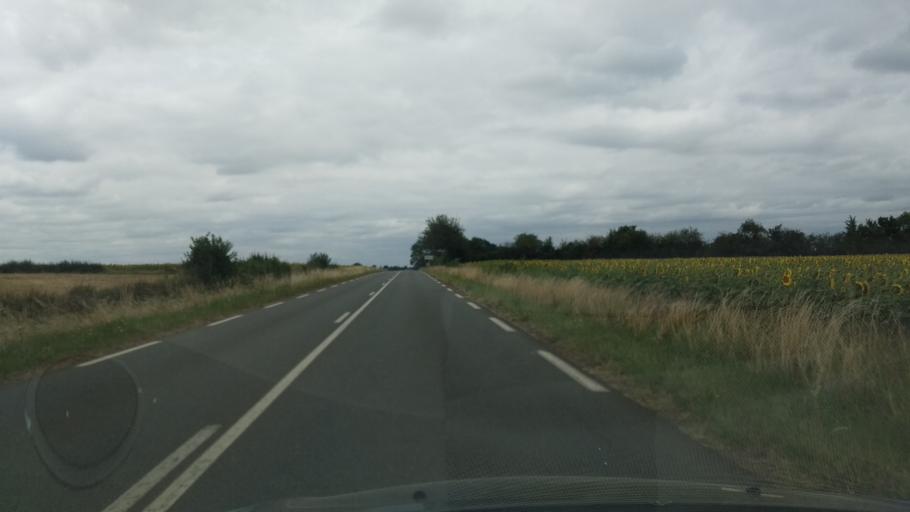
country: FR
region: Poitou-Charentes
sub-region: Departement de la Vienne
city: La Villedieu-du-Clain
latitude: 46.4313
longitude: 0.3759
